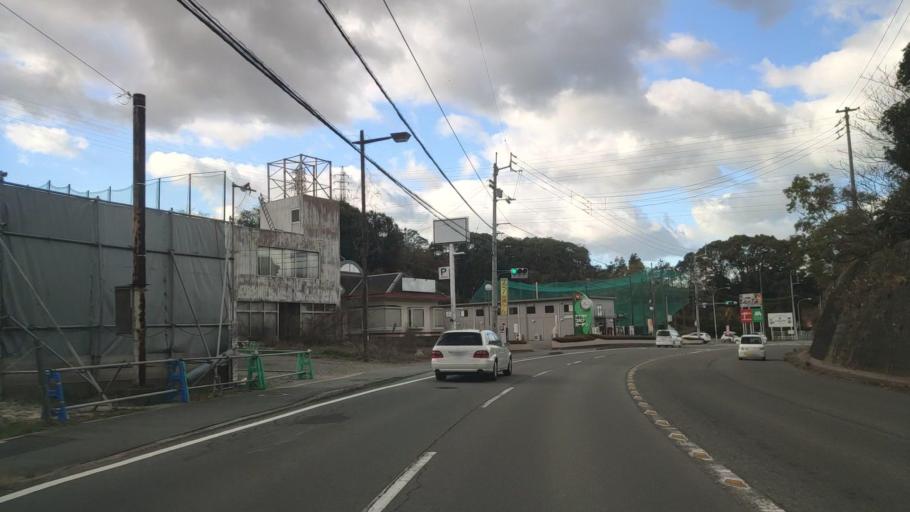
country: JP
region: Ehime
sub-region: Shikoku-chuo Shi
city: Matsuyama
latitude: 33.8562
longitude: 132.7358
